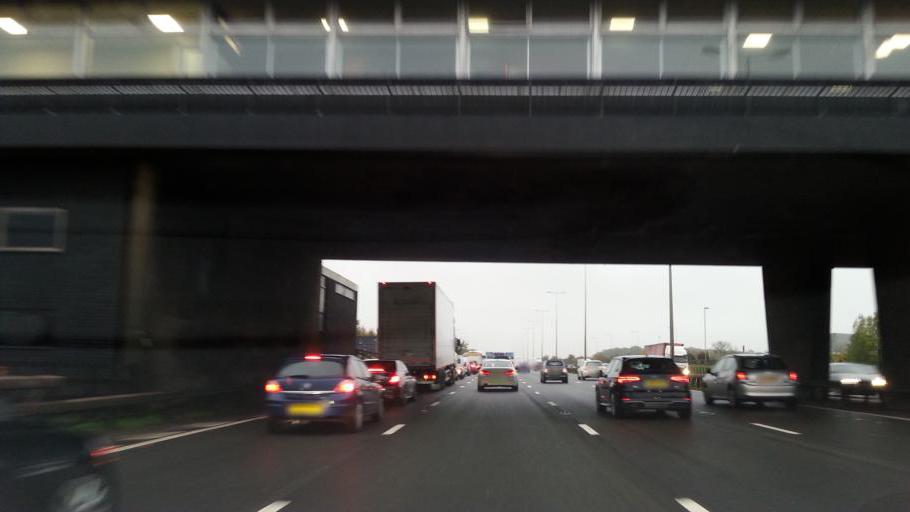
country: GB
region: England
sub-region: Leicestershire
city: Kirby Muxloe
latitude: 52.6194
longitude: -1.2057
